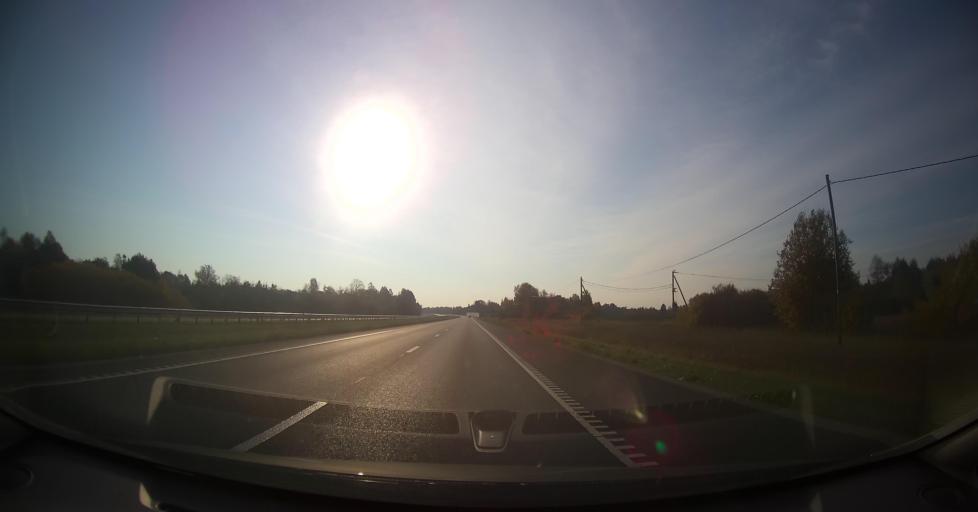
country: EE
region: Harju
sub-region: Rae vald
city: Vaida
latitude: 59.3082
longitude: 24.9390
